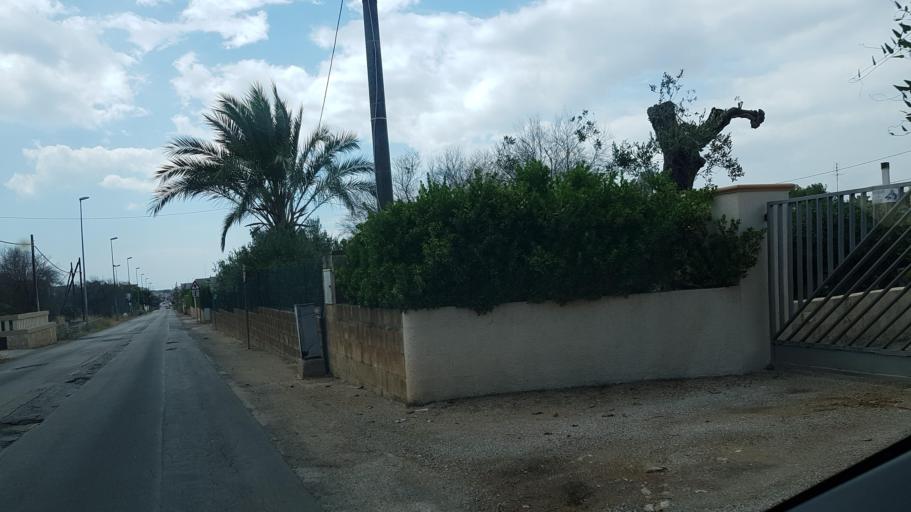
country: IT
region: Apulia
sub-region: Provincia di Lecce
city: Taurisano
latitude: 39.9589
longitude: 18.2254
